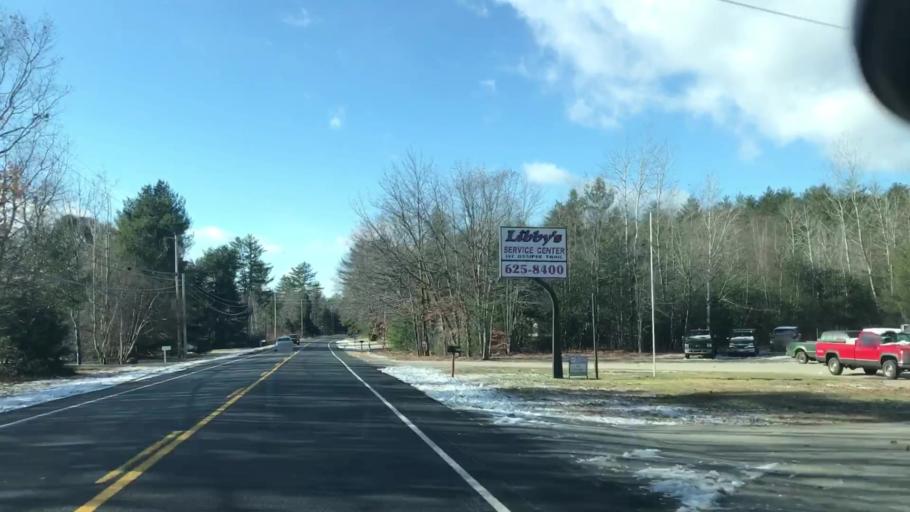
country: US
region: Maine
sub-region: Oxford County
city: Porter
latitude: 43.8038
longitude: -70.9006
